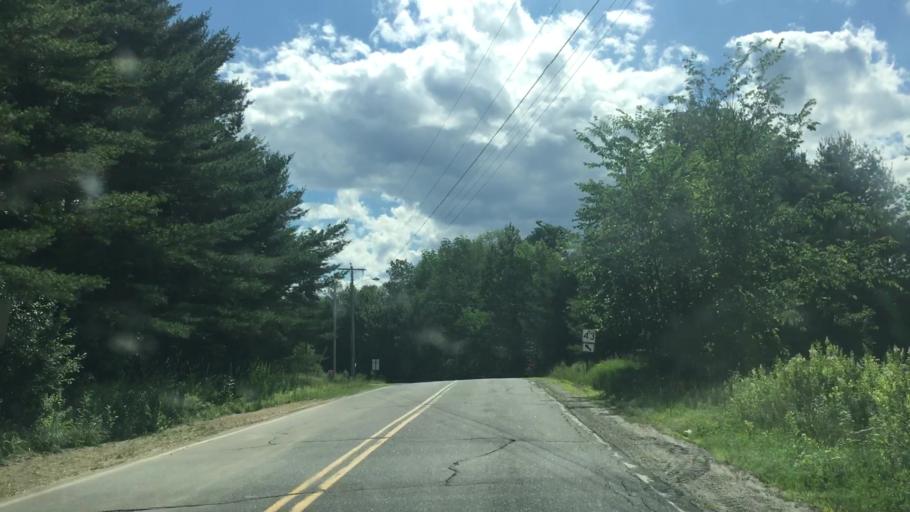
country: US
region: Maine
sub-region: Franklin County
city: Farmington
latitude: 44.7029
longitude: -70.1075
